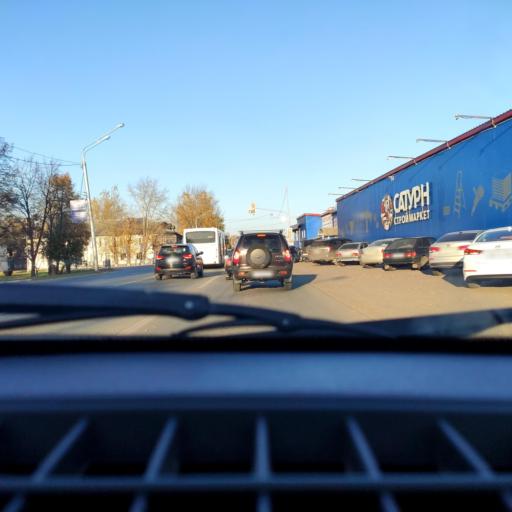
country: RU
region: Bashkortostan
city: Avdon
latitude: 54.6949
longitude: 55.8267
